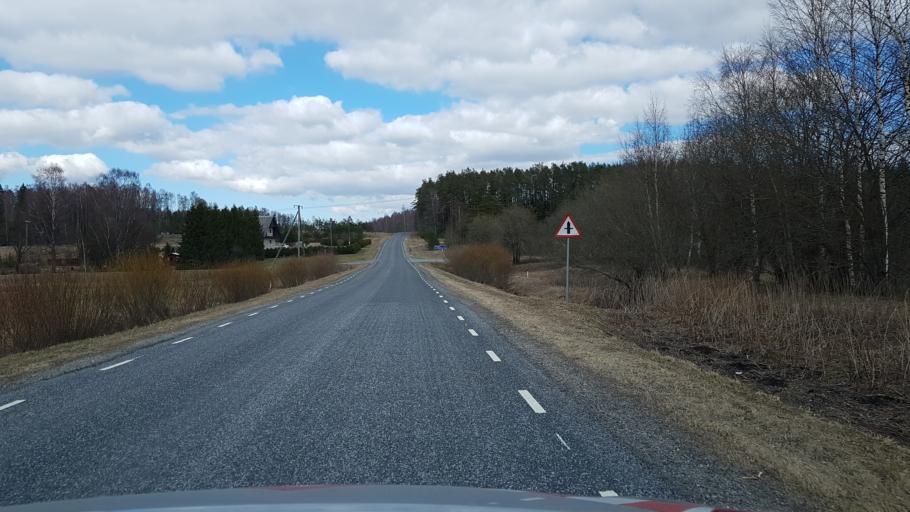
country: EE
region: Laeaene-Virumaa
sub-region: Tamsalu vald
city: Tamsalu
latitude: 59.2096
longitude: 26.1483
